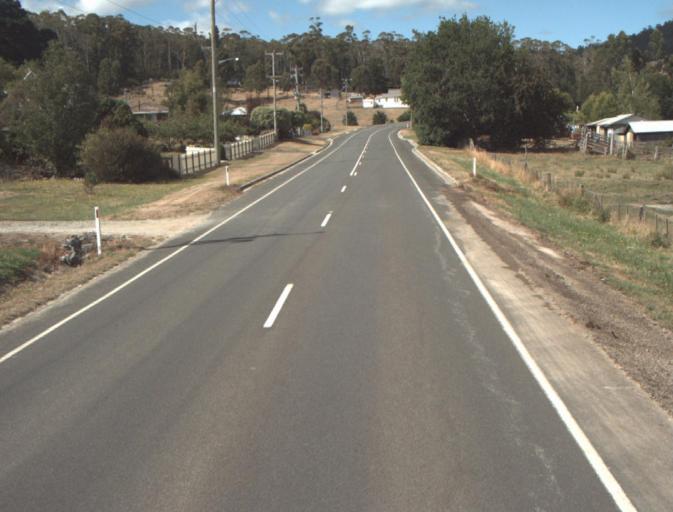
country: AU
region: Tasmania
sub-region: Launceston
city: Mayfield
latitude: -41.2603
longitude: 147.2180
